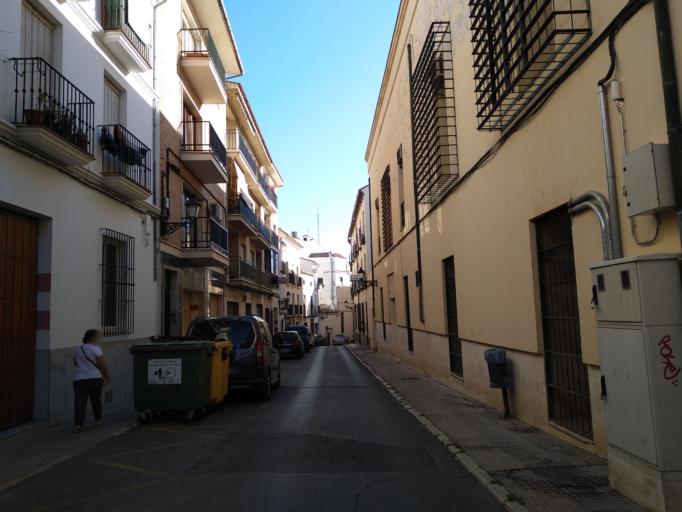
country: ES
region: Andalusia
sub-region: Provincia de Malaga
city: Antequera
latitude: 37.0179
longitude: -4.5629
